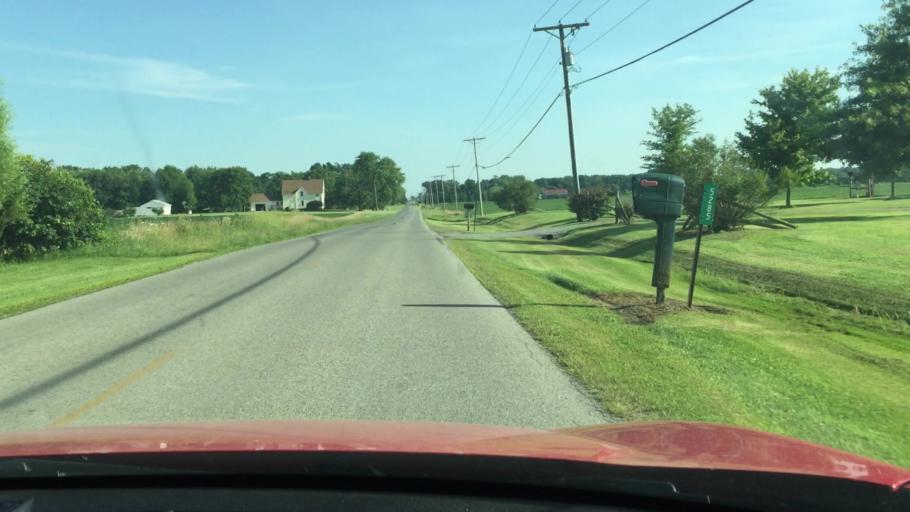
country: US
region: Ohio
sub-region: Hardin County
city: Ada
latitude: 40.7433
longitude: -83.8424
